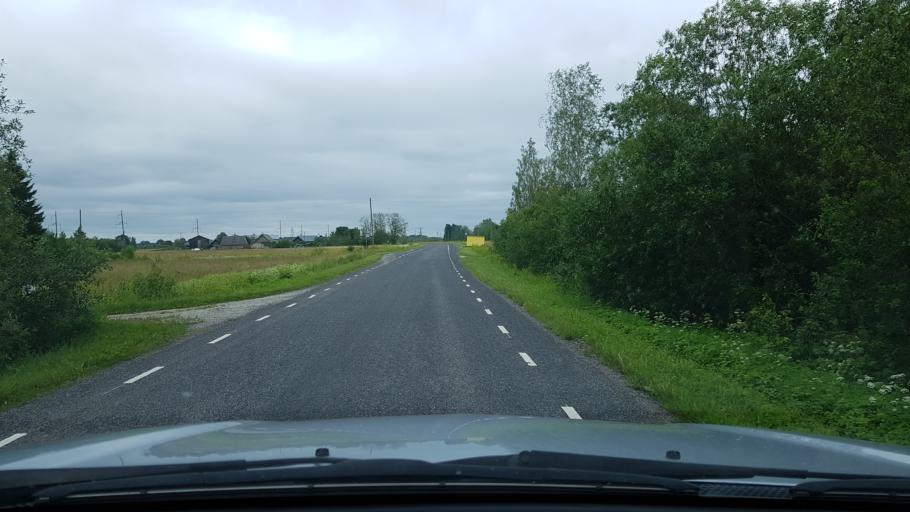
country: EE
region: Ida-Virumaa
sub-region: Narva-Joesuu linn
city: Narva-Joesuu
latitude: 59.3702
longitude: 28.0860
